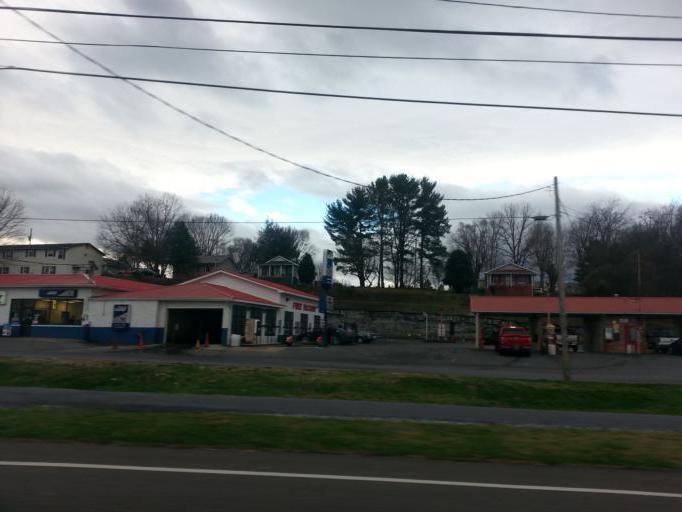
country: US
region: Tennessee
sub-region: Carter County
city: Elizabethton
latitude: 36.3508
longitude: -82.2347
